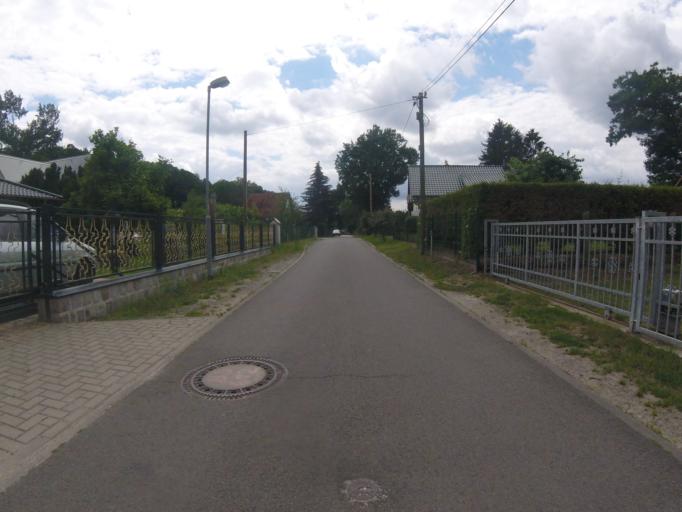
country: DE
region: Brandenburg
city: Bestensee
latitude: 52.2387
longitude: 13.6440
